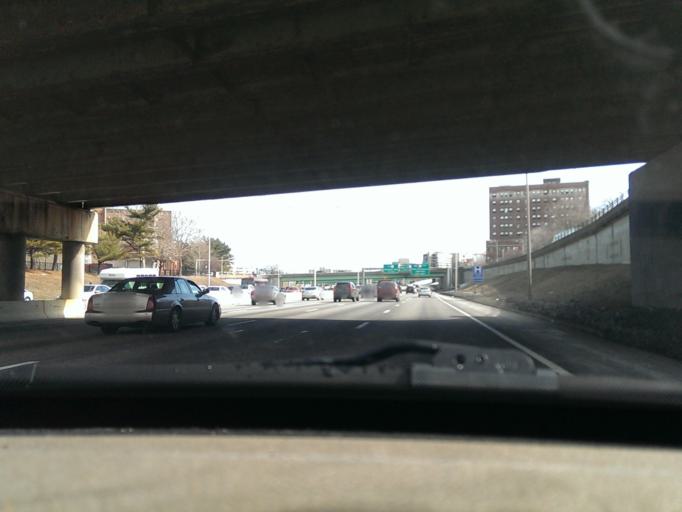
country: US
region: Rhode Island
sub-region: Providence County
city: Providence
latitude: 41.8191
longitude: -71.4189
